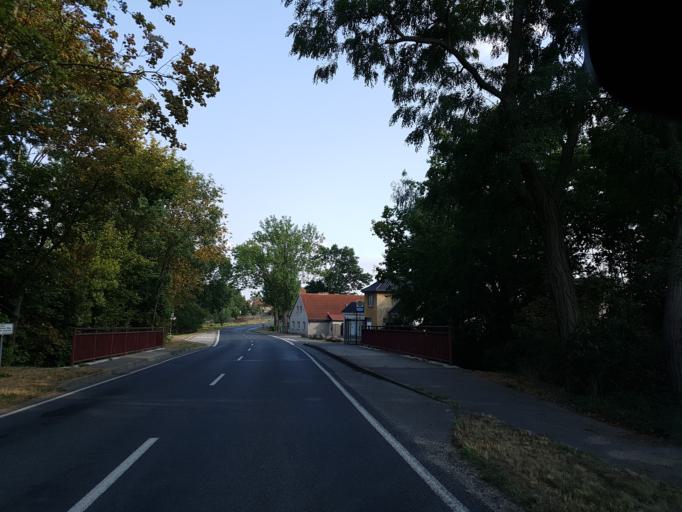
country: DE
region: Saxony
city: Elsnig
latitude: 51.6160
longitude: 12.9104
